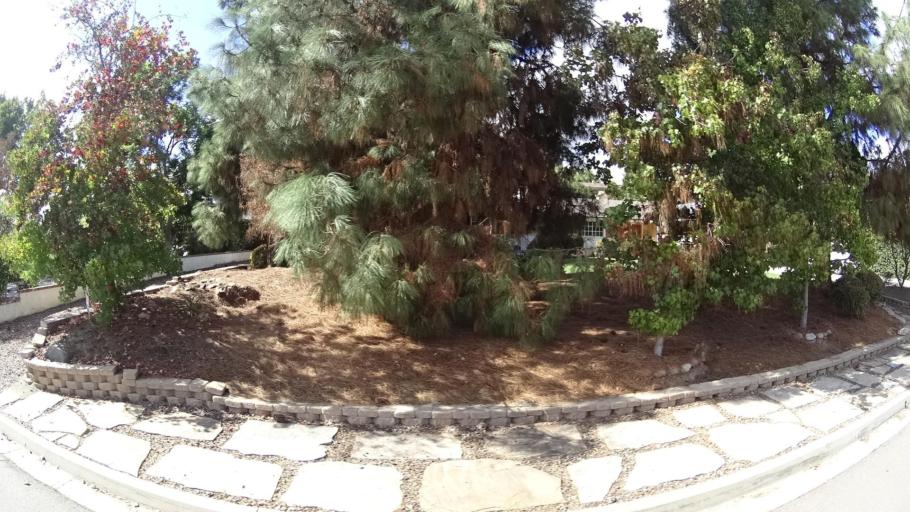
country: US
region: California
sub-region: San Diego County
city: Rancho San Diego
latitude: 32.7640
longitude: -116.9444
